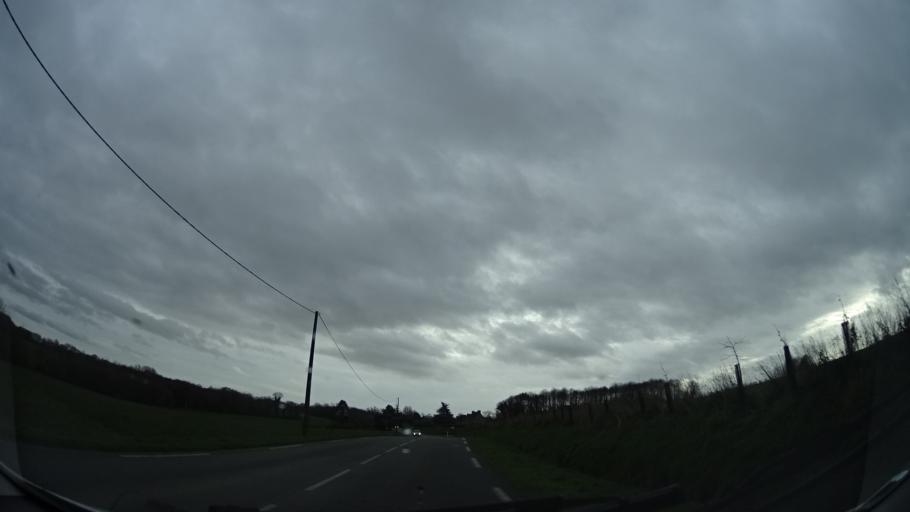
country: FR
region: Brittany
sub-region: Departement des Cotes-d'Armor
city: Les Champs-Geraux
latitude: 48.4146
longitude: -1.9973
